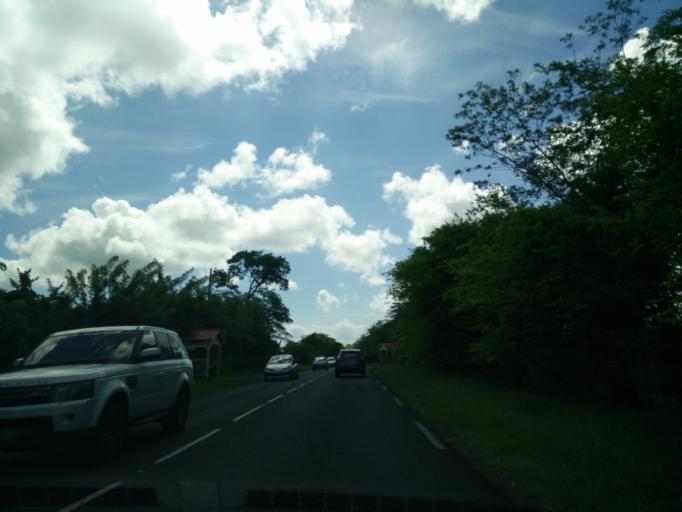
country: MQ
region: Martinique
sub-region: Martinique
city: Les Trois-Ilets
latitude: 14.5263
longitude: -60.9890
